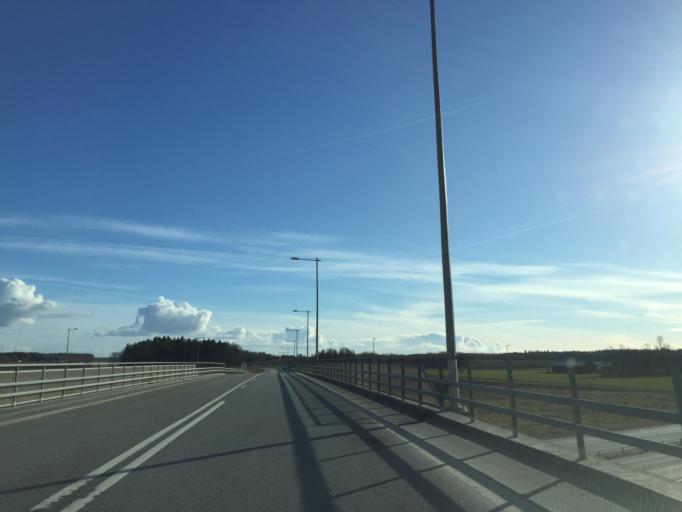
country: SE
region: OErebro
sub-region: Orebro Kommun
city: Vintrosa
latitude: 59.2475
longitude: 15.0551
